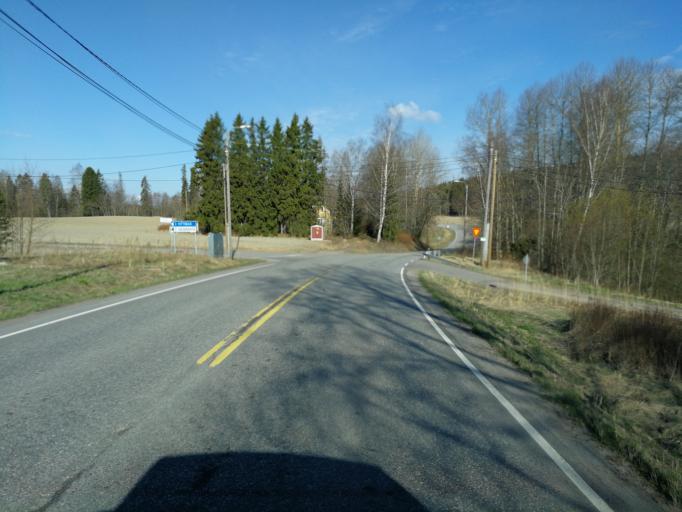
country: FI
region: Uusimaa
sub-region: Helsinki
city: Kirkkonummi
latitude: 60.2040
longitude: 24.5027
